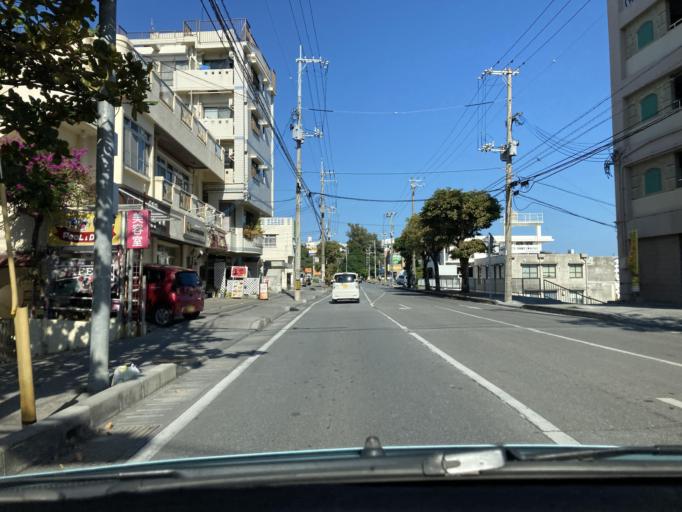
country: JP
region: Okinawa
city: Ginowan
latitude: 26.2325
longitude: 127.7247
